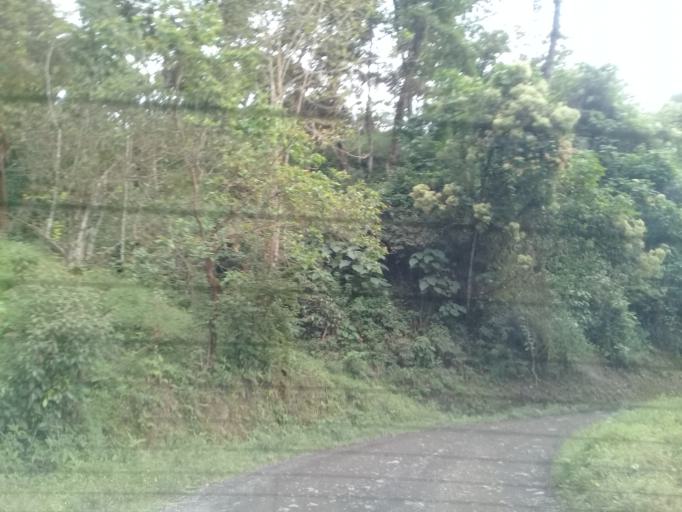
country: CO
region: Cundinamarca
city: Quipile
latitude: 4.7232
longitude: -74.5576
